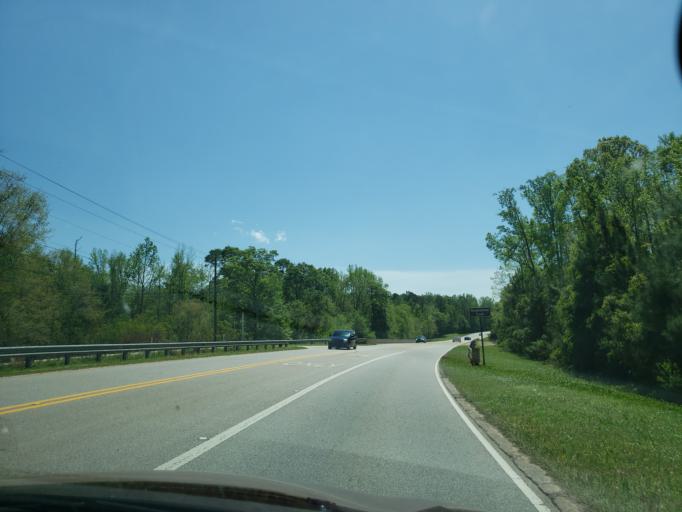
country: US
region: Alabama
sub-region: Lee County
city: Auburn
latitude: 32.6433
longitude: -85.5054
